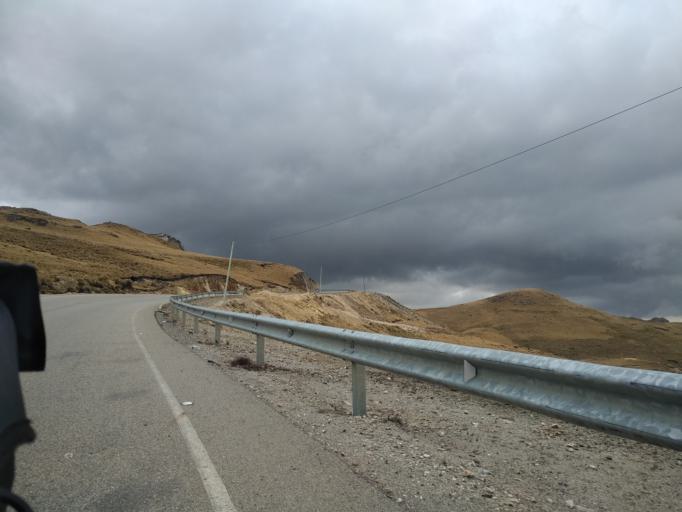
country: PE
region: La Libertad
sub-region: Provincia de Santiago de Chuco
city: Quiruvilca
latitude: -7.9886
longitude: -78.2820
